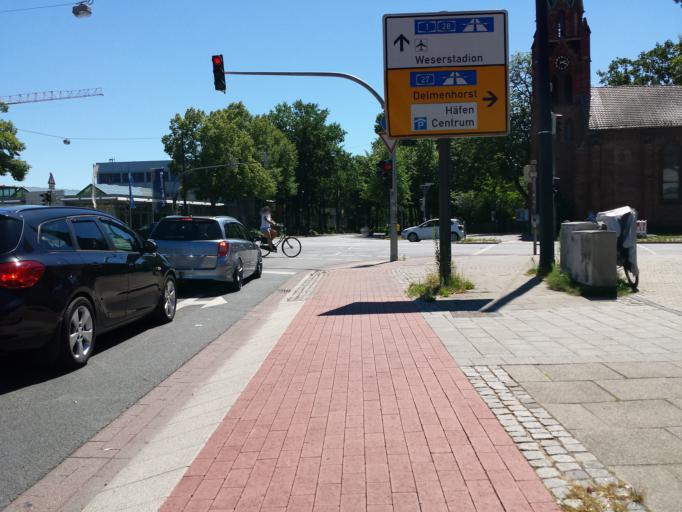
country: DE
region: Bremen
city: Bremen
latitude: 53.0731
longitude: 8.8569
